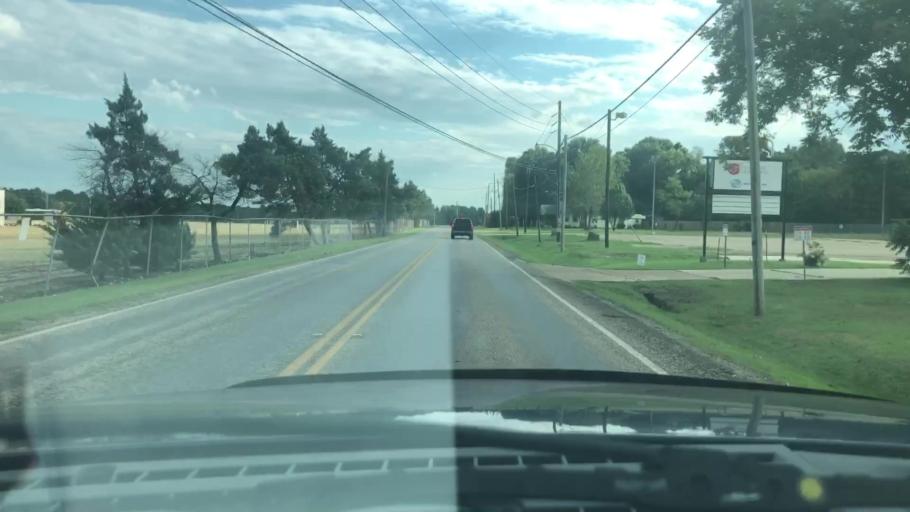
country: US
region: Texas
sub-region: Bowie County
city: Texarkana
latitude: 33.3962
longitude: -94.0646
